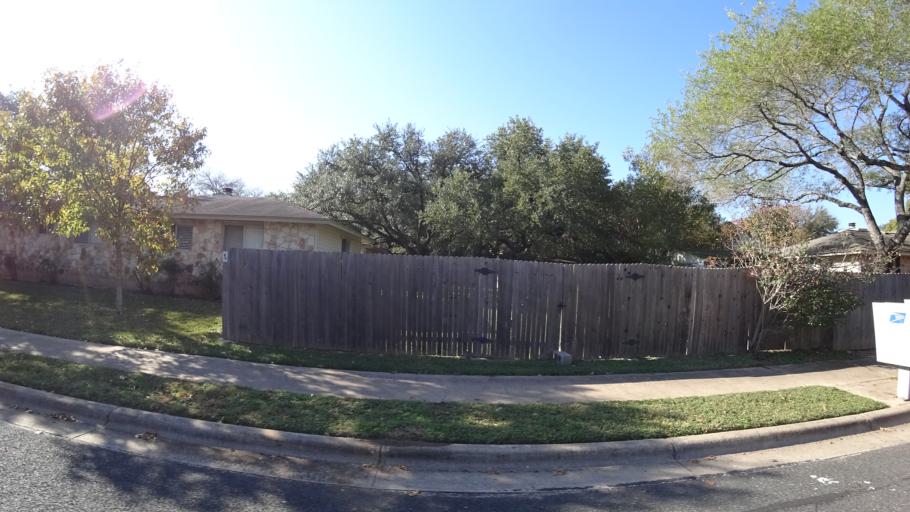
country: US
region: Texas
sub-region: Travis County
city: Shady Hollow
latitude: 30.2257
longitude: -97.8373
